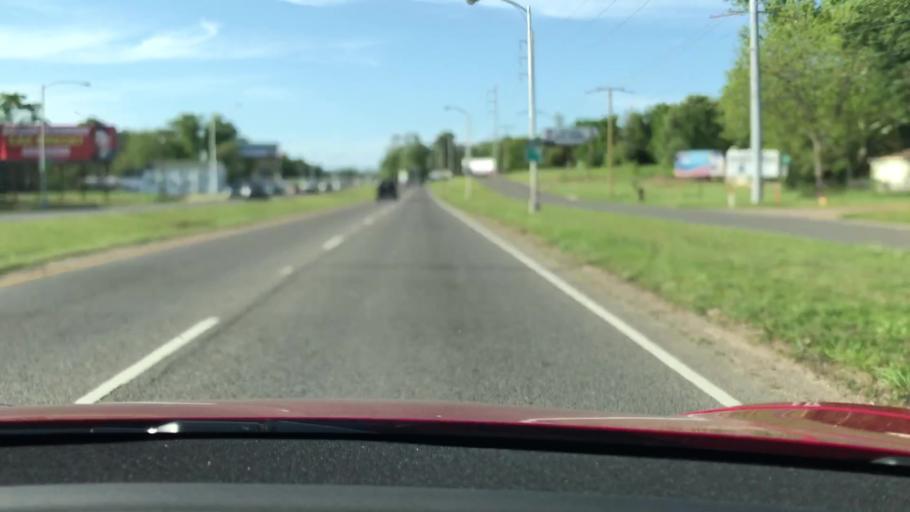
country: US
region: Louisiana
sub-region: Bossier Parish
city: Bossier City
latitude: 32.4896
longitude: -93.7242
